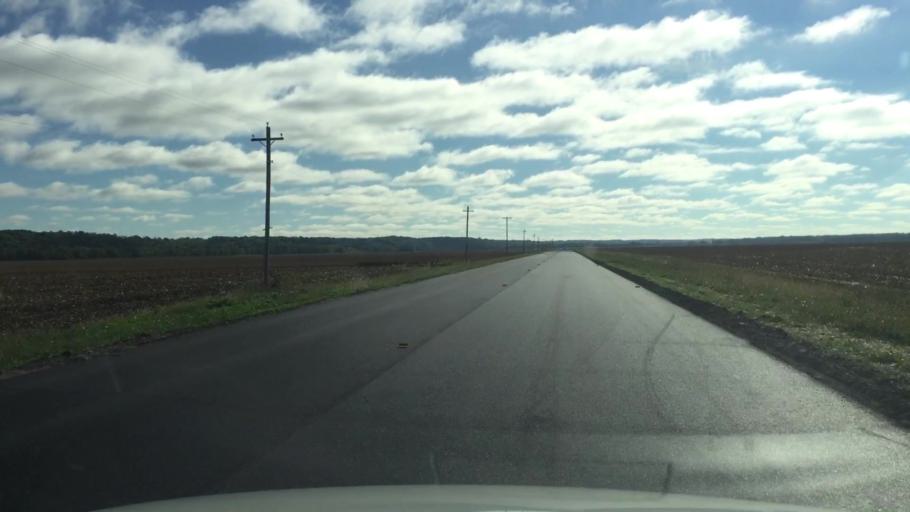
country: US
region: Missouri
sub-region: Howard County
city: New Franklin
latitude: 38.9952
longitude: -92.6596
